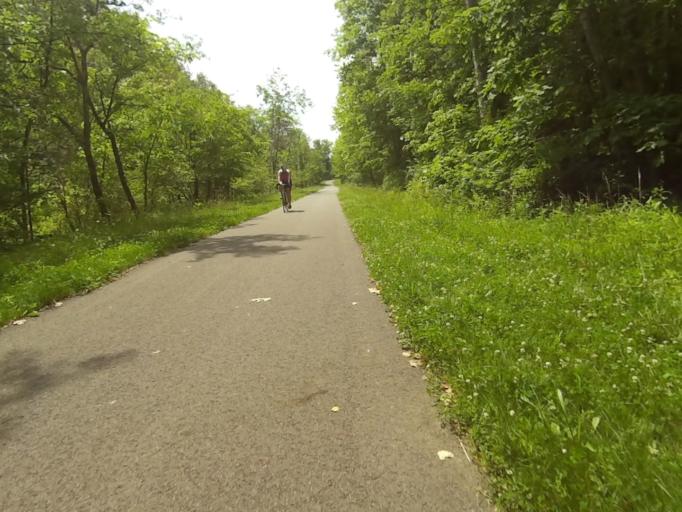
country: US
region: Ohio
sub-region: Summit County
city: Boston Heights
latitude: 41.2649
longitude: -81.5250
